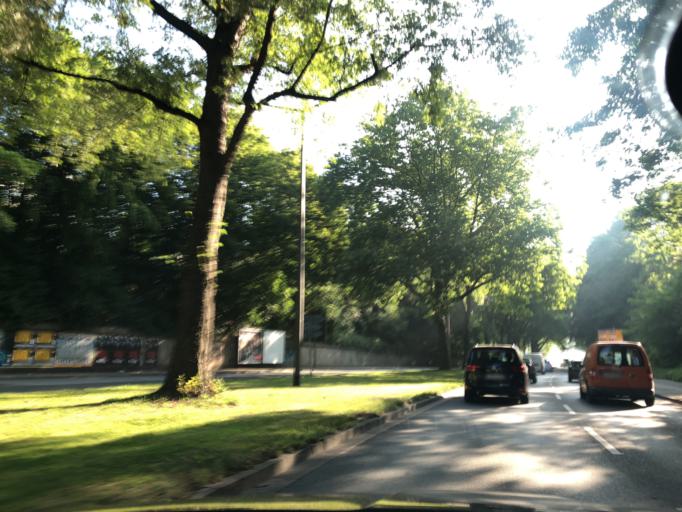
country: DE
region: North Rhine-Westphalia
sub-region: Regierungsbezirk Dusseldorf
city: Essen
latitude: 51.4665
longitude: 7.0035
